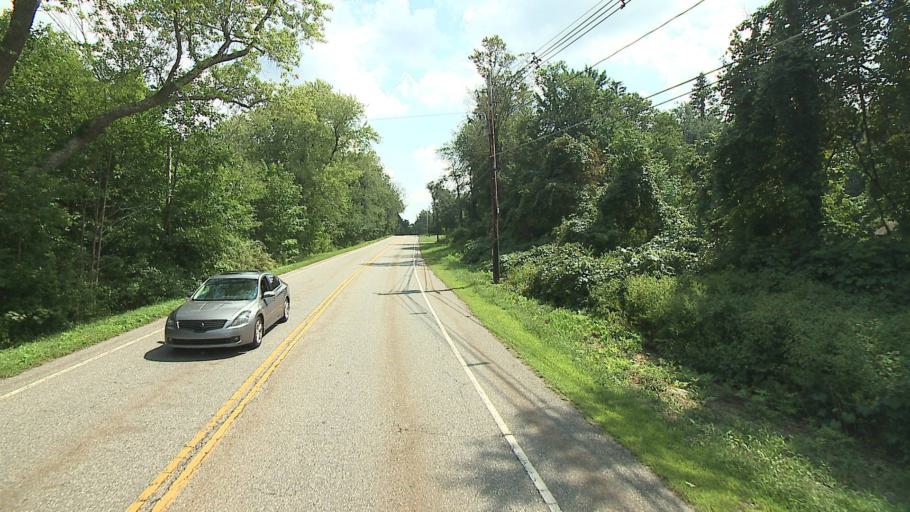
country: US
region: Connecticut
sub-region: Litchfield County
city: Bethlehem Village
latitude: 41.6814
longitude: -73.1666
